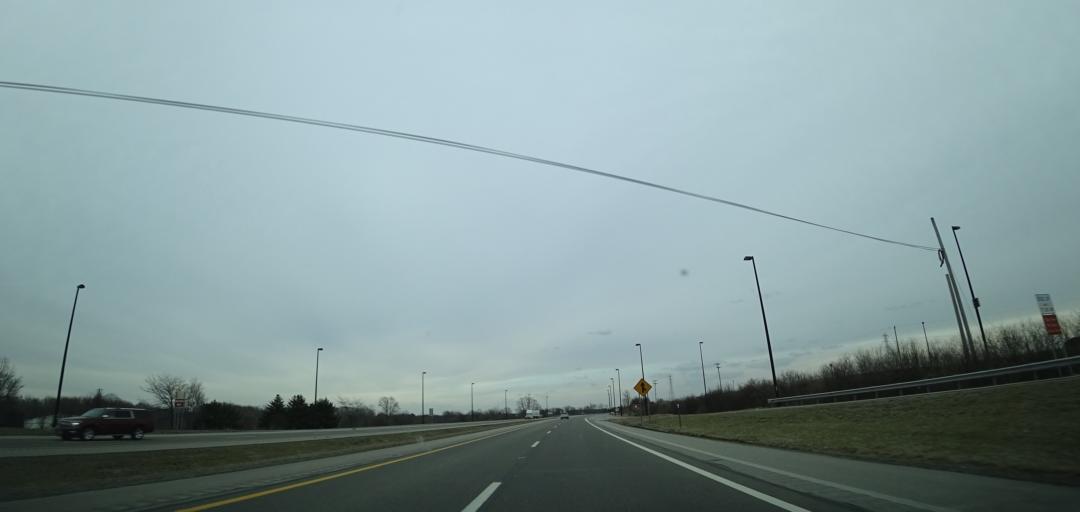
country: US
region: Ohio
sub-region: Mahoning County
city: New Middletown
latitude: 40.9390
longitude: -80.5843
